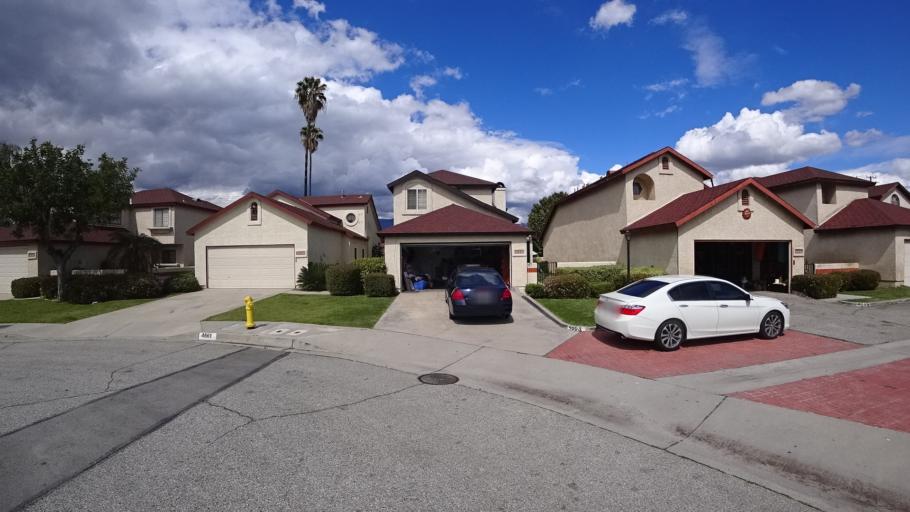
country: US
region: California
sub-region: Los Angeles County
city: Baldwin Park
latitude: 34.0972
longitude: -117.9616
